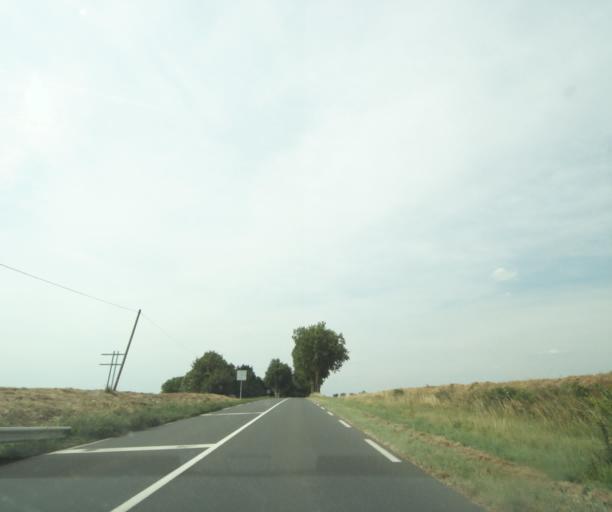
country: FR
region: Centre
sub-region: Departement d'Indre-et-Loire
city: Neuille-Pont-Pierre
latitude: 47.5652
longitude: 0.5492
